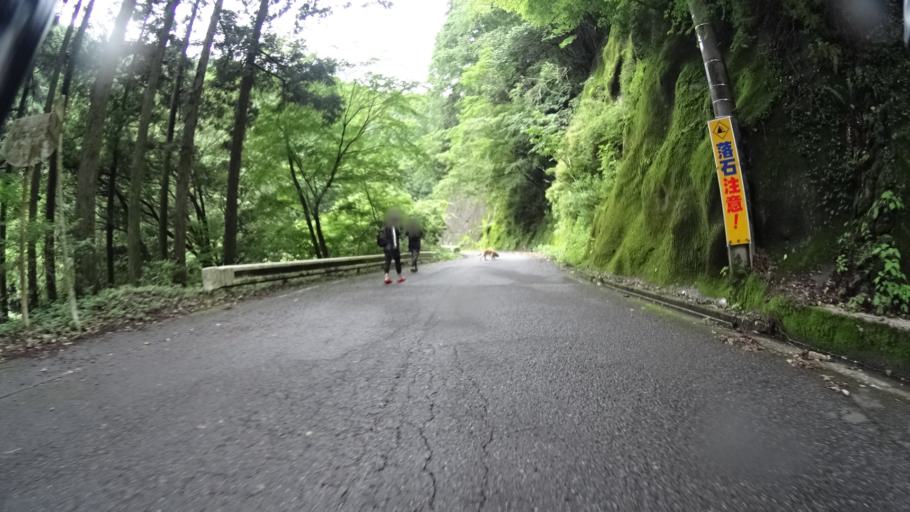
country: JP
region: Tokyo
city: Ome
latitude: 35.8752
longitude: 139.1547
